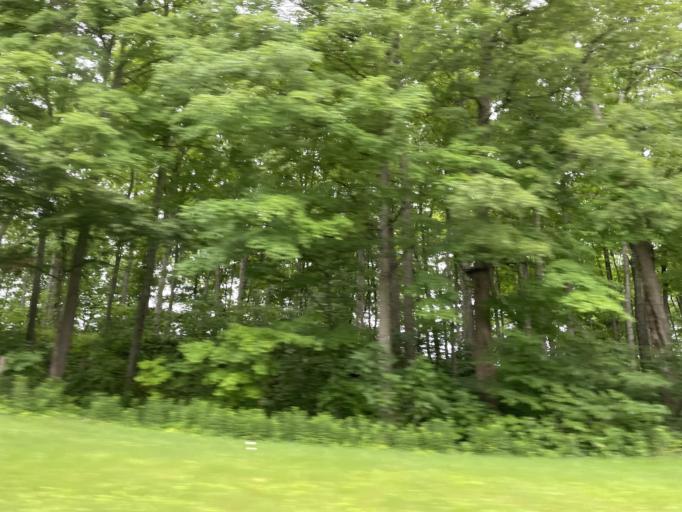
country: CA
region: Ontario
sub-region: Wellington County
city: Guelph
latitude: 43.4448
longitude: -80.2550
